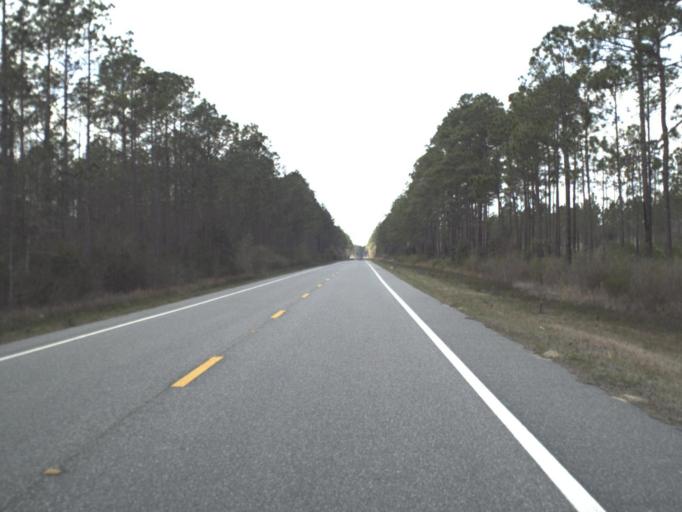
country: US
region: Florida
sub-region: Franklin County
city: Apalachicola
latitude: 29.8425
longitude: -84.9529
